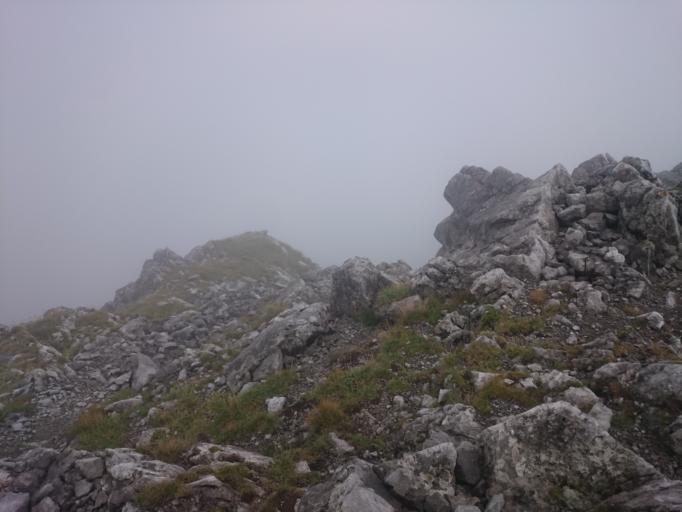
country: AT
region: Tyrol
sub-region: Politischer Bezirk Innsbruck Land
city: Gnadenwald
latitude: 47.4272
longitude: 11.5123
